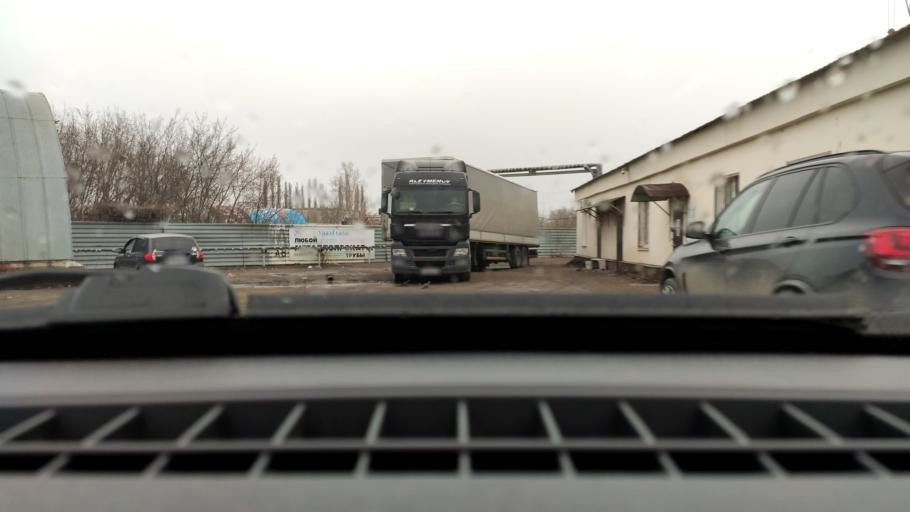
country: RU
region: Bashkortostan
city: Ufa
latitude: 54.7969
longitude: 56.0822
